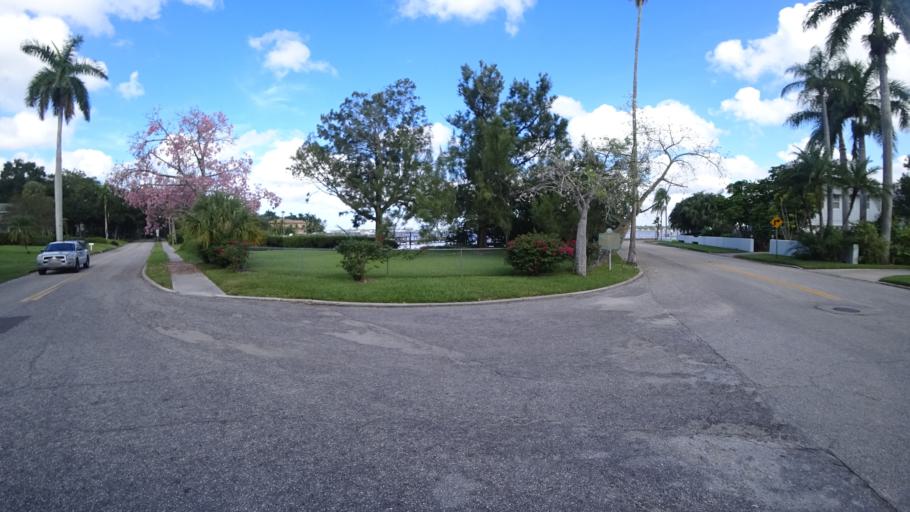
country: US
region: Florida
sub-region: Manatee County
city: Bradenton
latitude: 27.4998
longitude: -82.5875
